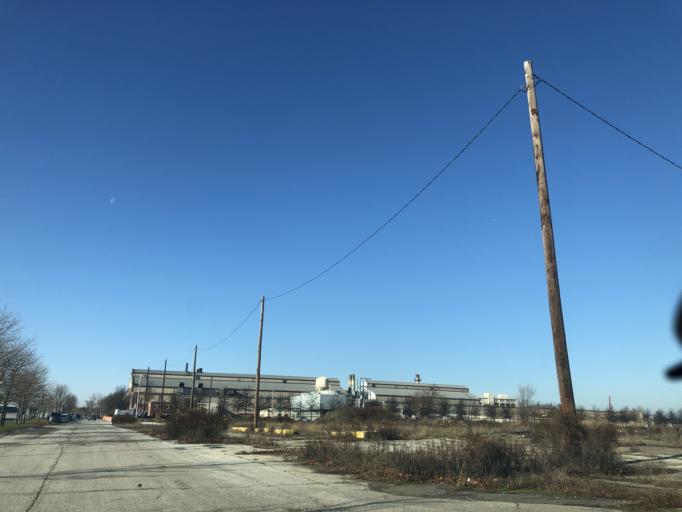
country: US
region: New Jersey
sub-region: Gloucester County
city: National Park
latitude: 39.8877
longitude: -75.1636
